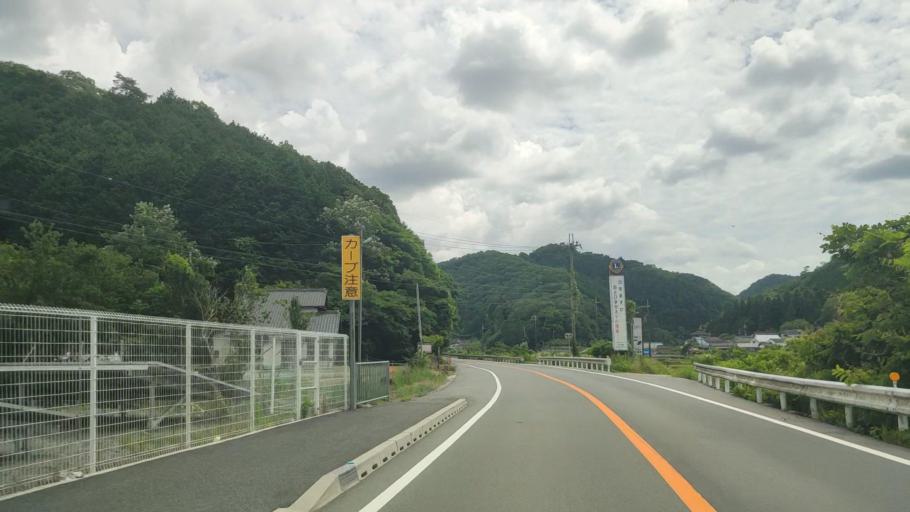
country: JP
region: Hyogo
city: Yamazakicho-nakabirose
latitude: 34.9677
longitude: 134.4477
